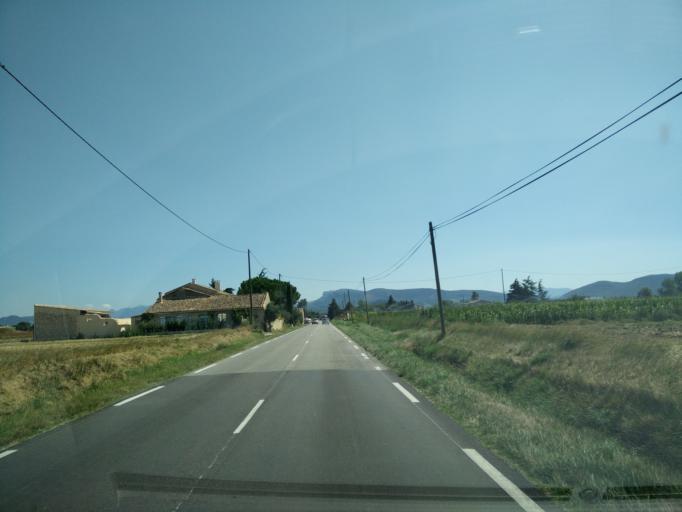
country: FR
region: Rhone-Alpes
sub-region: Departement de la Drome
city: La Begude-de-Mazenc
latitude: 44.5527
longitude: 4.8797
